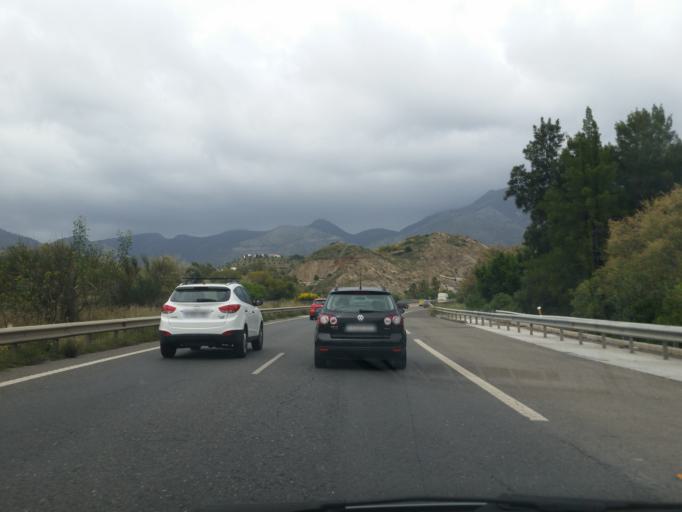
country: ES
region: Andalusia
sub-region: Provincia de Malaga
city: Mijas
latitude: 36.5713
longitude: -4.6229
